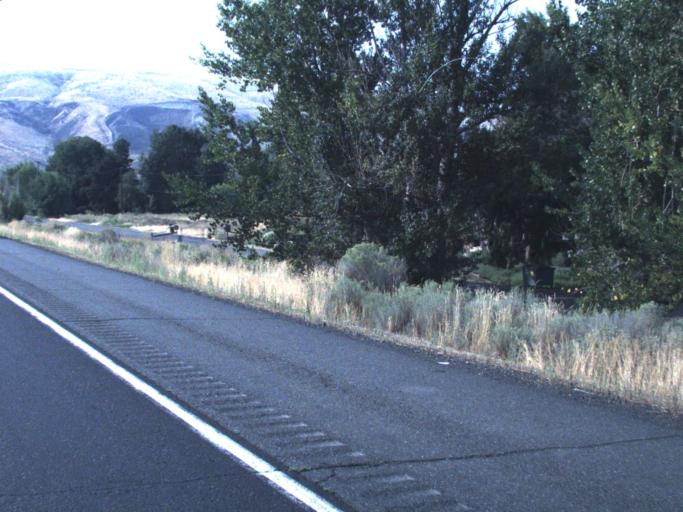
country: US
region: Washington
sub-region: Yakima County
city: Selah
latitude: 46.6566
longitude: -120.4970
